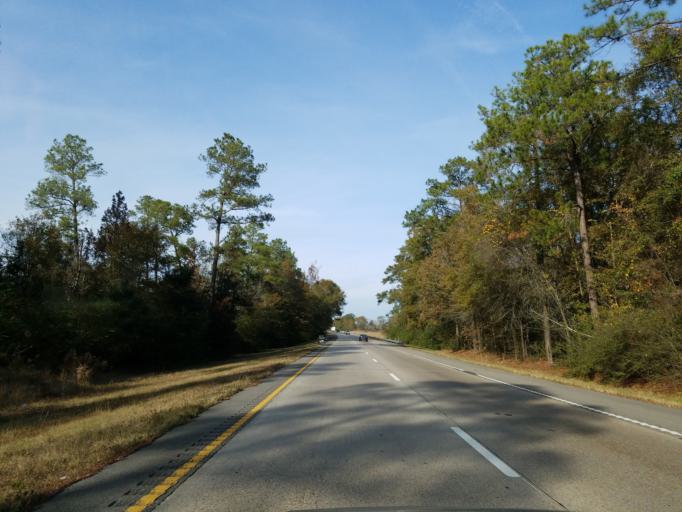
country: US
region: Mississippi
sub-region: Forrest County
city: Glendale
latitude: 31.4001
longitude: -89.3190
